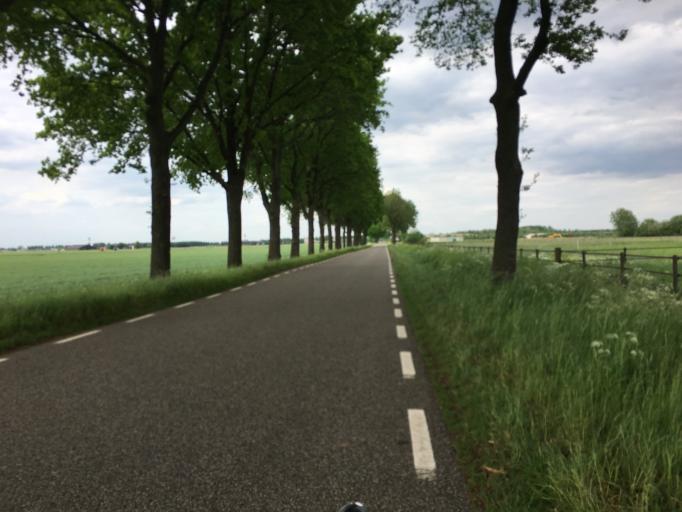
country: NL
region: Gelderland
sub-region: Gemeente Maasdriel
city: Hedel
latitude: 51.7086
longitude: 5.2379
